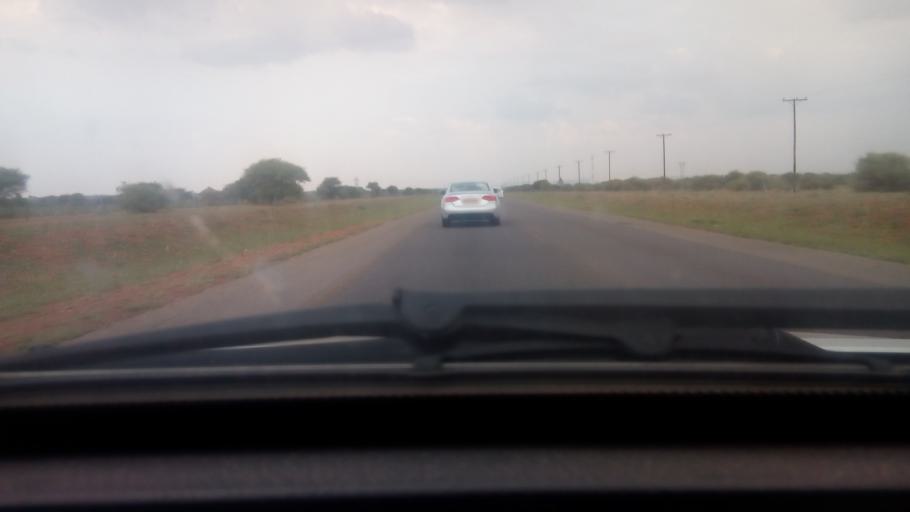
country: BW
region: Kweneng
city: Molepolole
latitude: -24.4567
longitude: 25.6526
